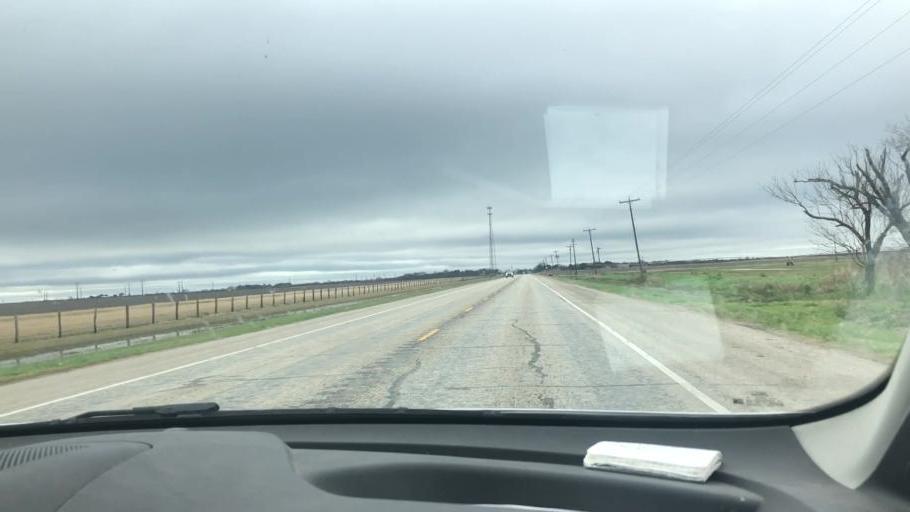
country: US
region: Texas
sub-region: Wharton County
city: Wharton
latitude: 29.2363
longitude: -96.0387
